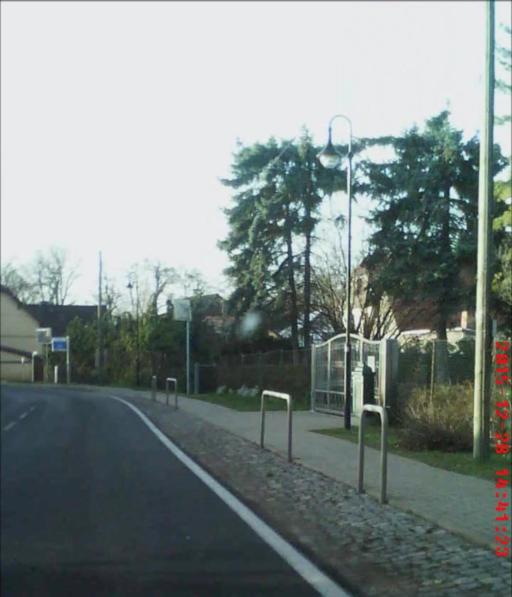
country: DE
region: Thuringia
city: Schwerstedt
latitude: 51.0714
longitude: 11.2951
